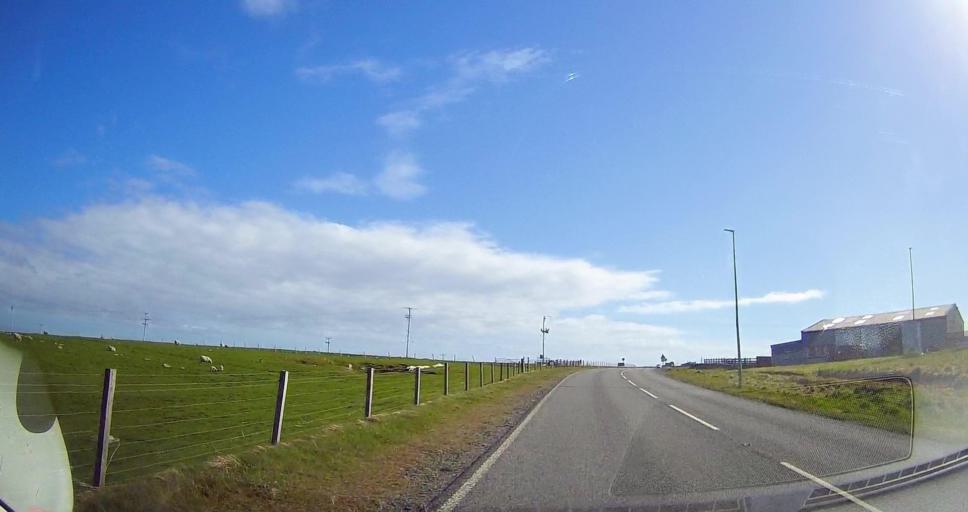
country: GB
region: Scotland
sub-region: Shetland Islands
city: Sandwick
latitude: 59.9194
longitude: -1.2993
